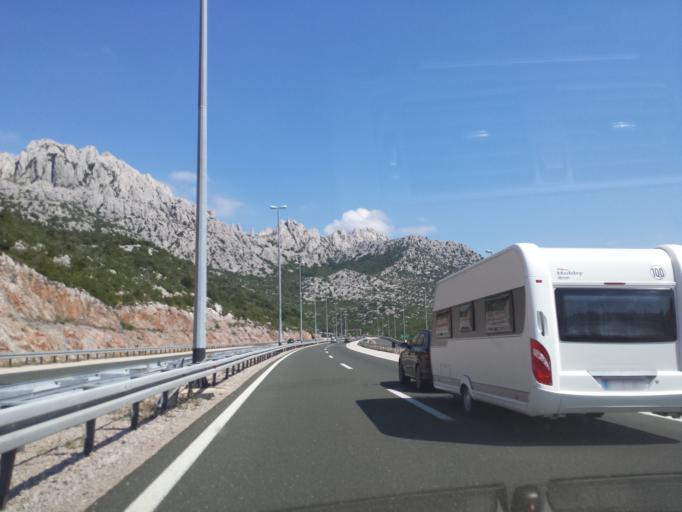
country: HR
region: Zadarska
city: Obrovac
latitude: 44.2513
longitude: 15.6392
